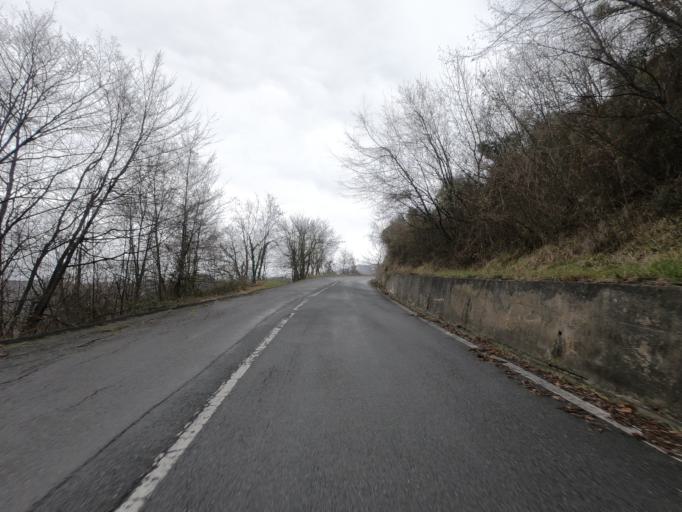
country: IT
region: Liguria
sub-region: Provincia di Imperia
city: Cesio
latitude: 44.0236
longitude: 7.9926
